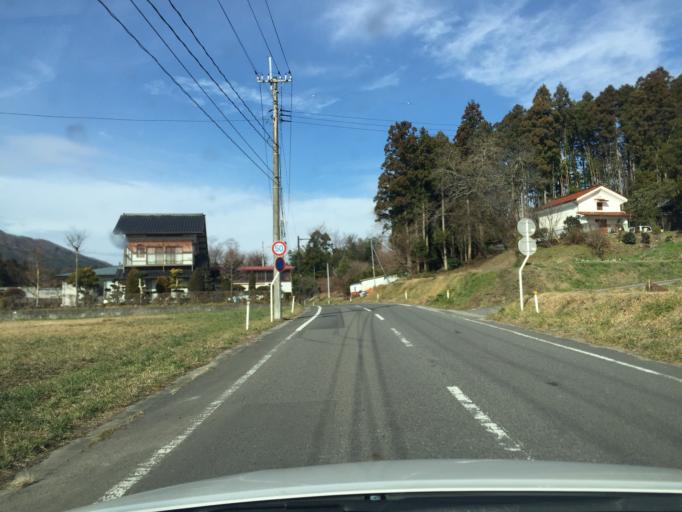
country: JP
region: Fukushima
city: Ishikawa
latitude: 37.2530
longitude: 140.5651
